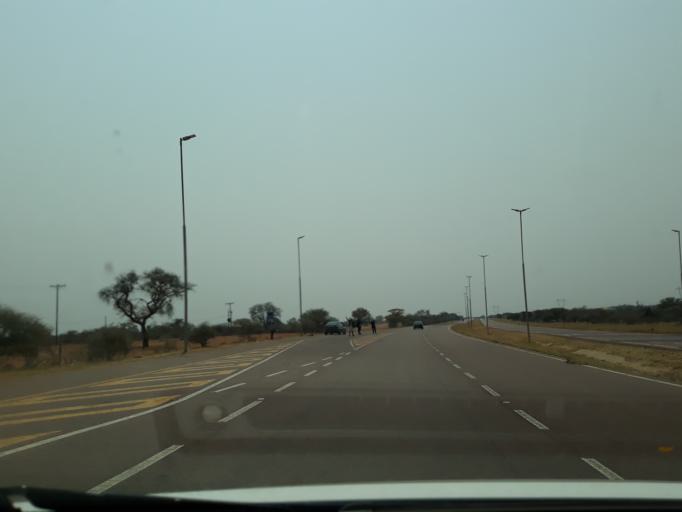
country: BW
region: Kgatleng
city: Mochudi
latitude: -24.3638
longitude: 26.0682
